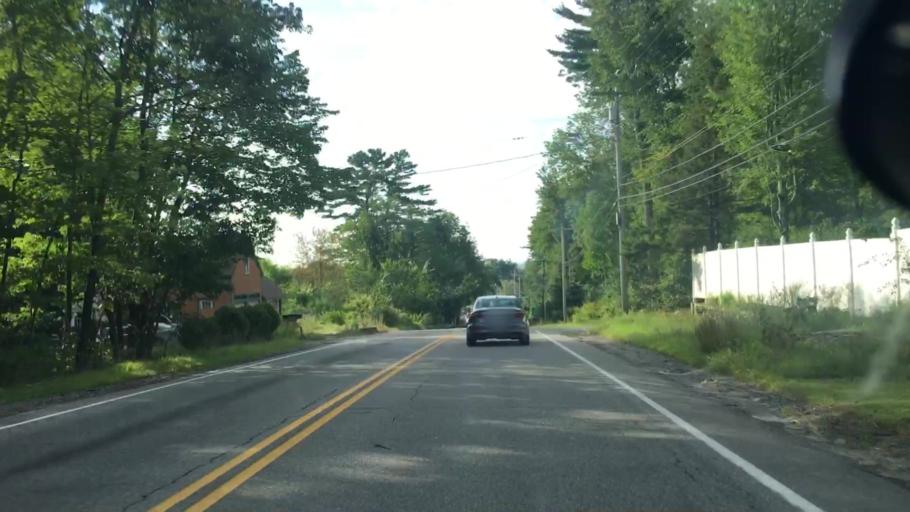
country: US
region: Maine
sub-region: Cumberland County
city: Westbrook
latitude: 43.7169
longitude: -70.3362
